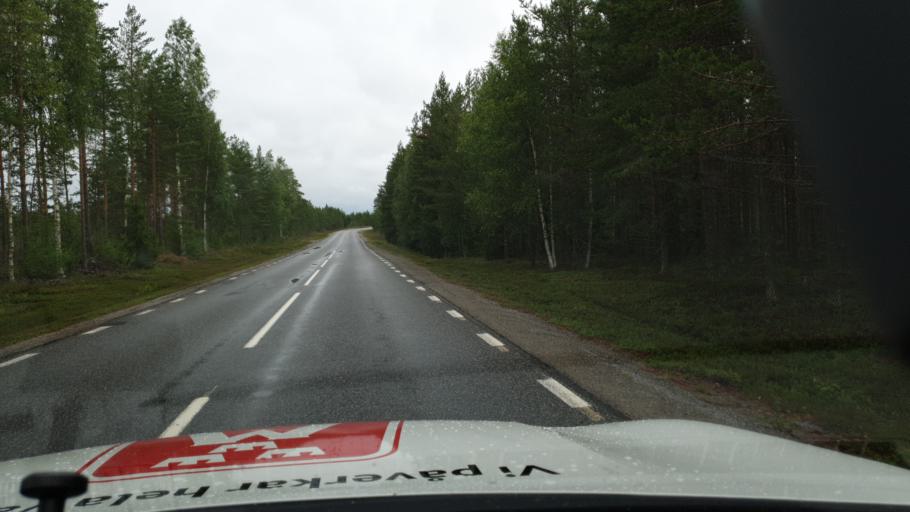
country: SE
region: Vaesterbotten
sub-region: Umea Kommun
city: Saevar
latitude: 63.9304
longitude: 20.5330
